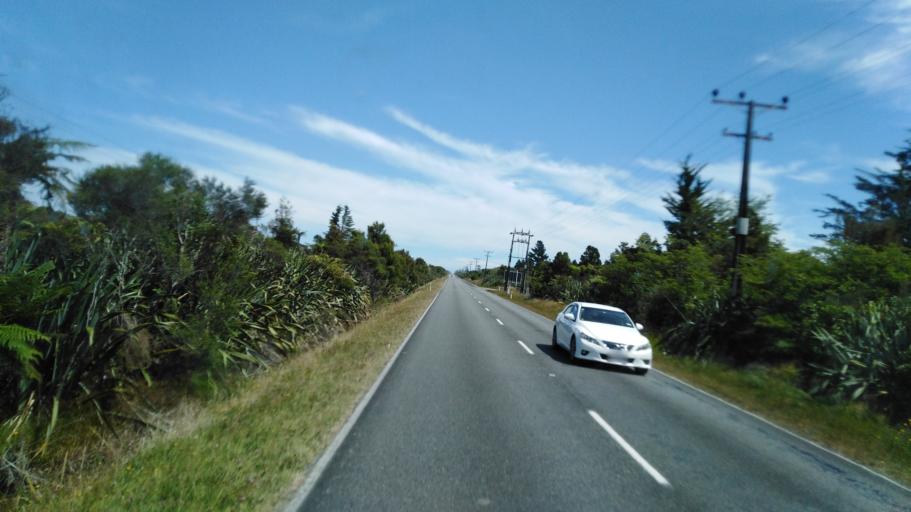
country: NZ
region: West Coast
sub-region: Buller District
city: Westport
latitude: -41.7434
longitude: 171.6904
